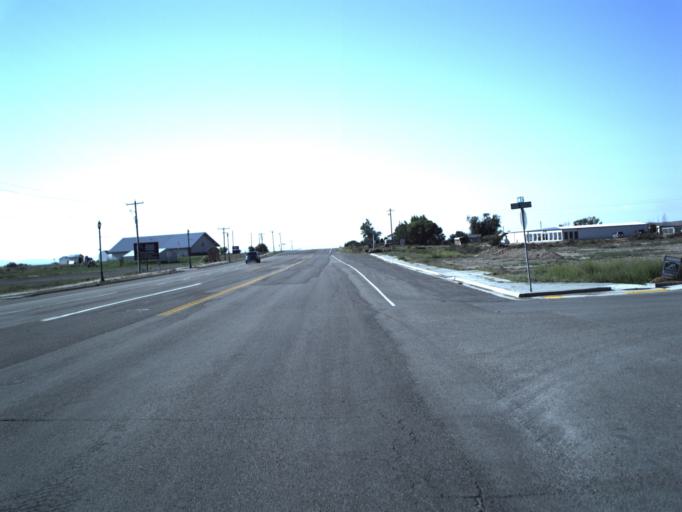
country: US
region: Utah
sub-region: Emery County
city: Huntington
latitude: 39.3213
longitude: -110.9646
